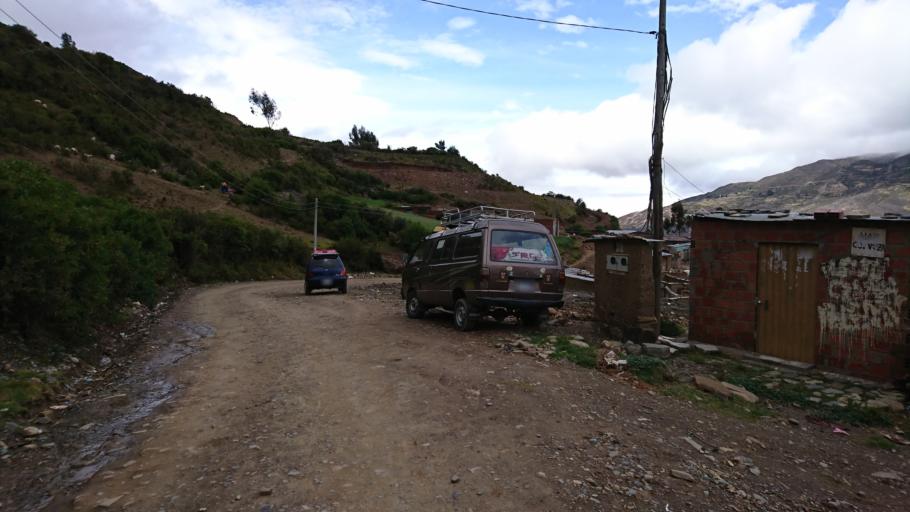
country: BO
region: La Paz
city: La Paz
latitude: -16.5442
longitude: -67.9957
